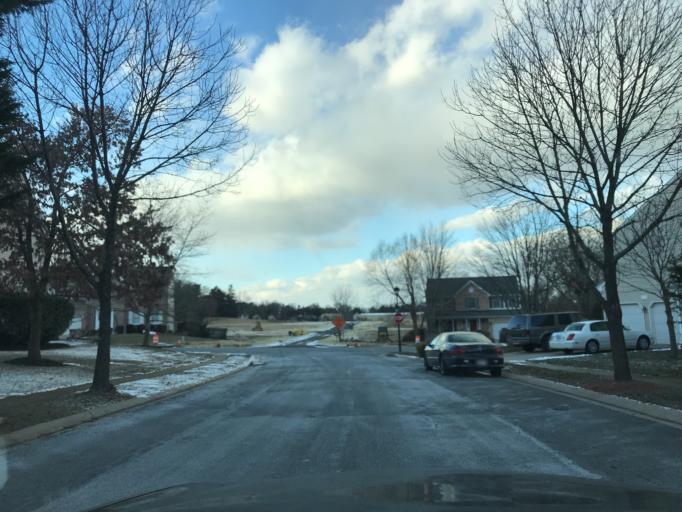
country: US
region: Maryland
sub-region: Harford County
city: Bel Air North
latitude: 39.5805
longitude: -76.3852
